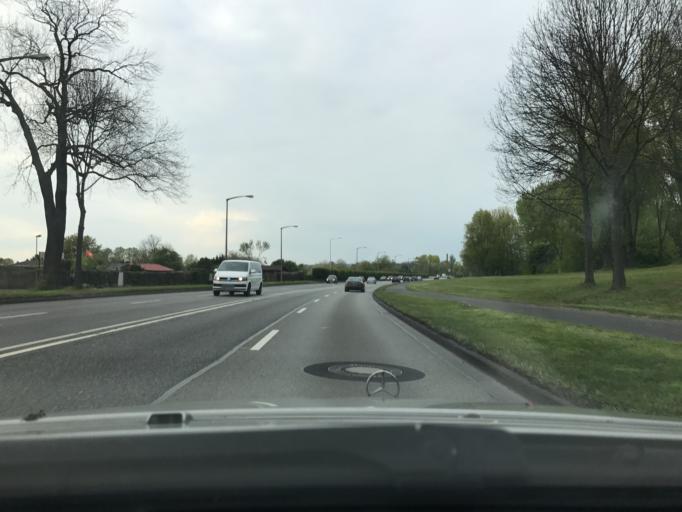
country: DE
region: Hesse
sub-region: Regierungsbezirk Kassel
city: Kassel
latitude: 51.2977
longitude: 9.5125
